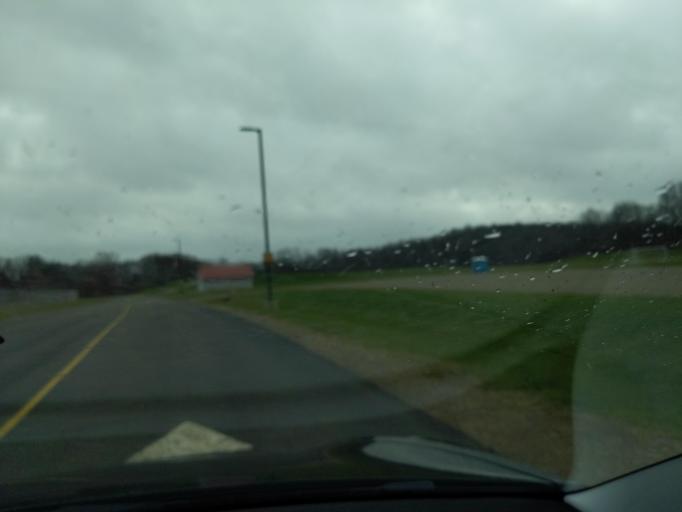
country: US
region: Michigan
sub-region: Jackson County
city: Spring Arbor
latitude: 42.2519
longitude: -84.5397
